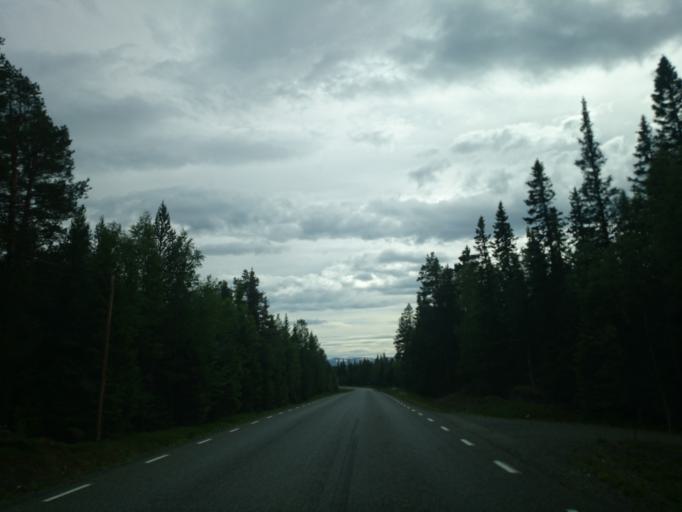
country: SE
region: Jaemtland
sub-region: Are Kommun
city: Are
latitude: 63.2146
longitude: 13.1623
